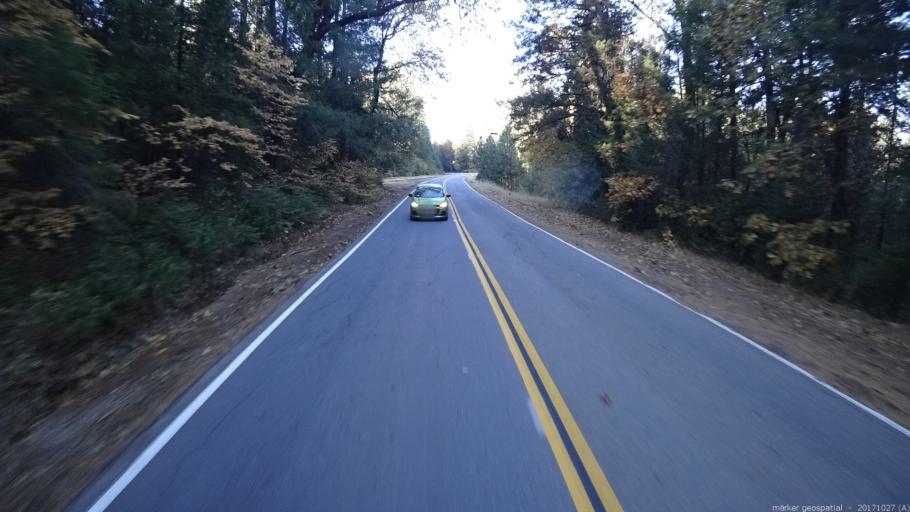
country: US
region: California
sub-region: Shasta County
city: Burney
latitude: 40.9907
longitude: -121.9224
